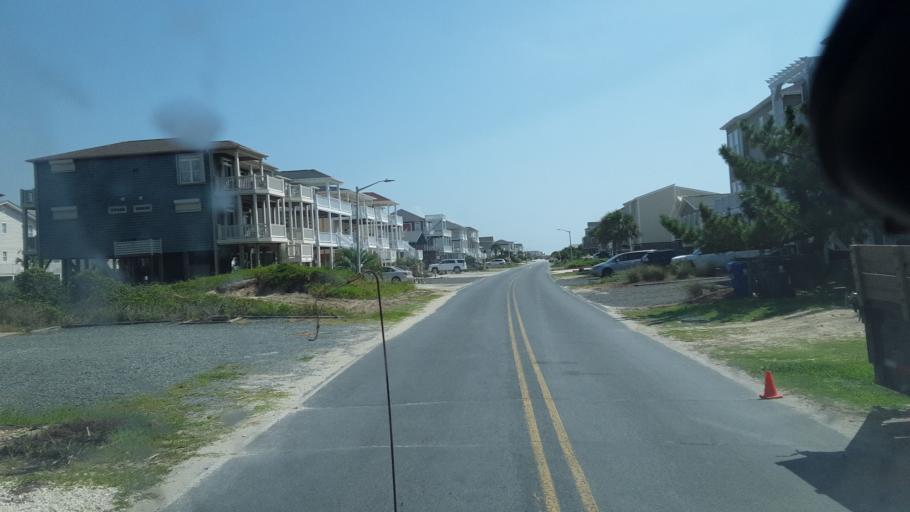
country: US
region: North Carolina
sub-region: Brunswick County
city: Shallotte
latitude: 33.8948
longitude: -78.4083
